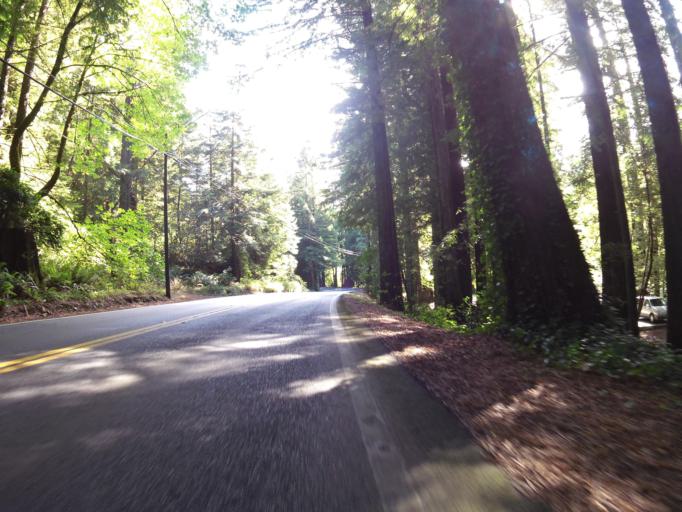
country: US
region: California
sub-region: Del Norte County
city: Bertsch-Oceanview
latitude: 41.8530
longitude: -124.1205
